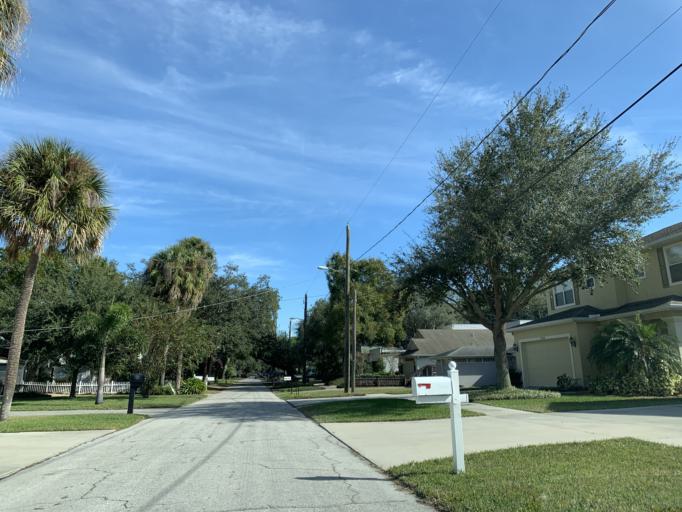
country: US
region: Florida
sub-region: Hillsborough County
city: Tampa
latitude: 27.8909
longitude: -82.4978
